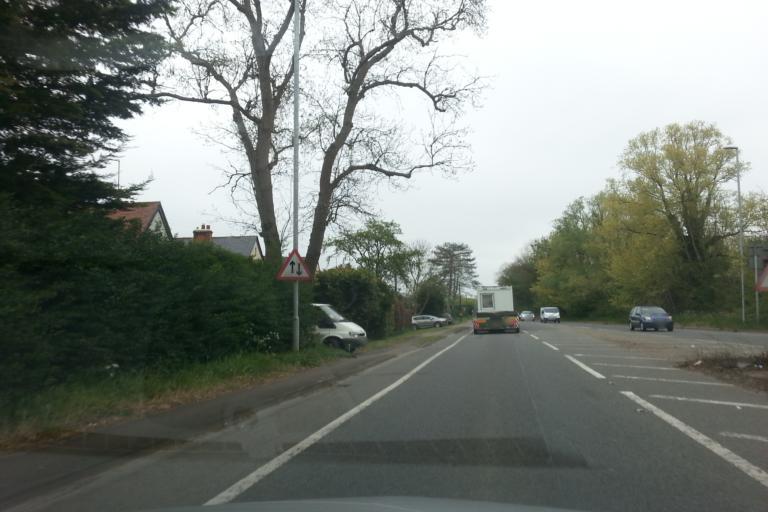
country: GB
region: England
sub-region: Cambridgeshire
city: Waterbeach
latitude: 52.2646
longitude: 0.1795
